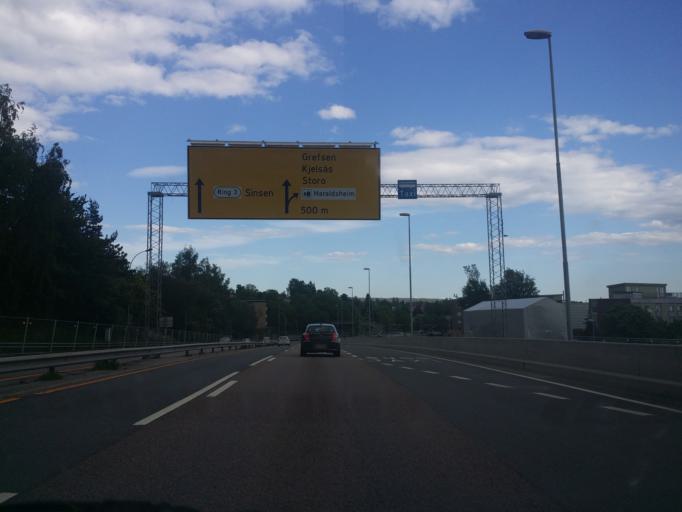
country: NO
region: Oslo
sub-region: Oslo
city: Oslo
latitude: 59.9522
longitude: 10.7722
